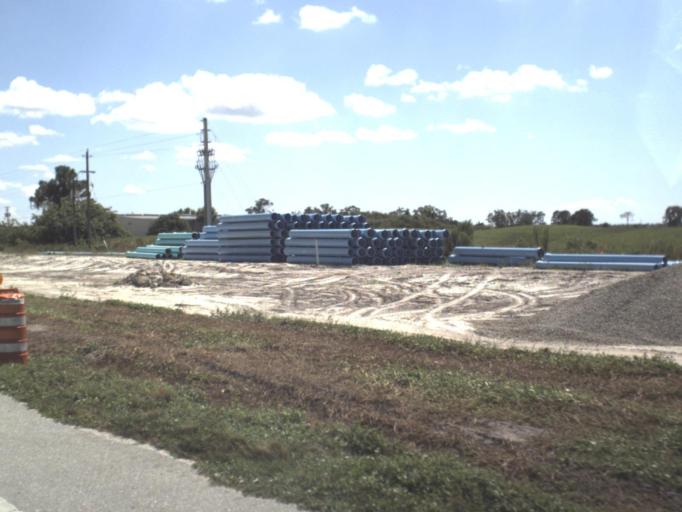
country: US
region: Florida
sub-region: Collier County
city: Lely Resort
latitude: 26.0347
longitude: -81.6544
